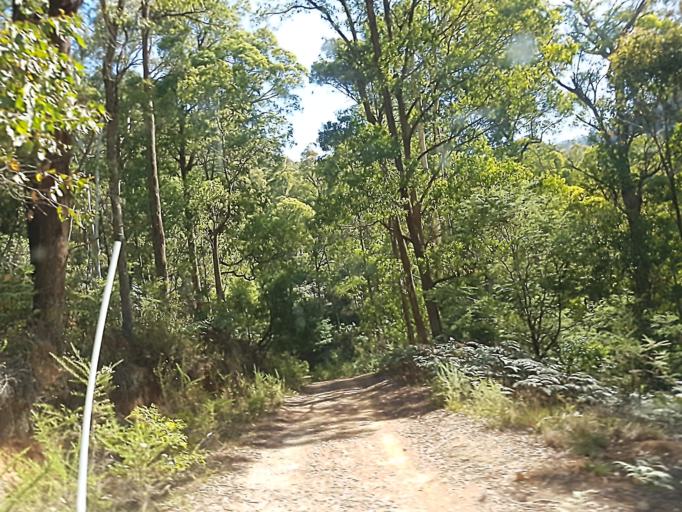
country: AU
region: Victoria
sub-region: Alpine
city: Mount Beauty
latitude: -36.9264
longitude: 147.0175
